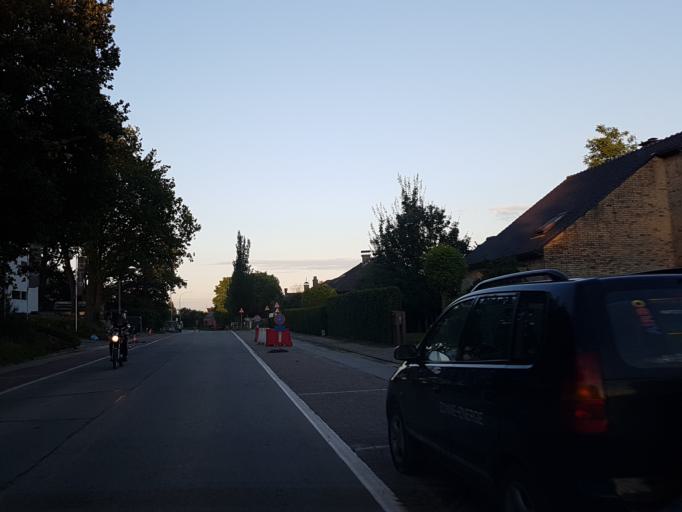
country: BE
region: Flanders
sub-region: Provincie Oost-Vlaanderen
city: Hamme
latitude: 51.1137
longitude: 4.1730
